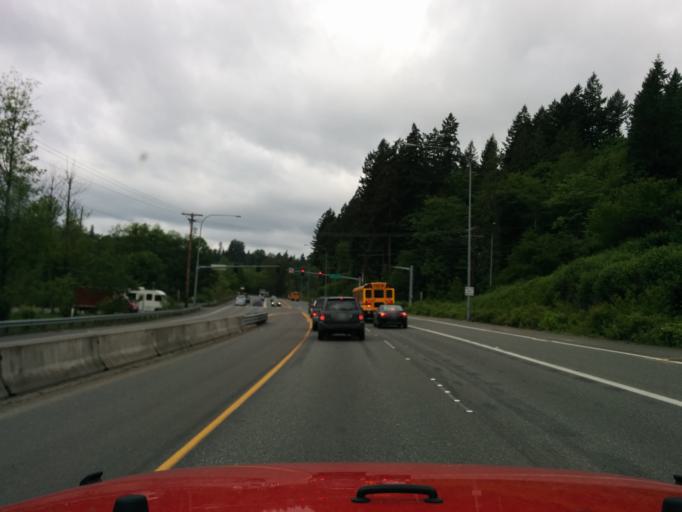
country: US
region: Washington
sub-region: King County
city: Sammamish
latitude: 47.6565
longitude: -122.0694
